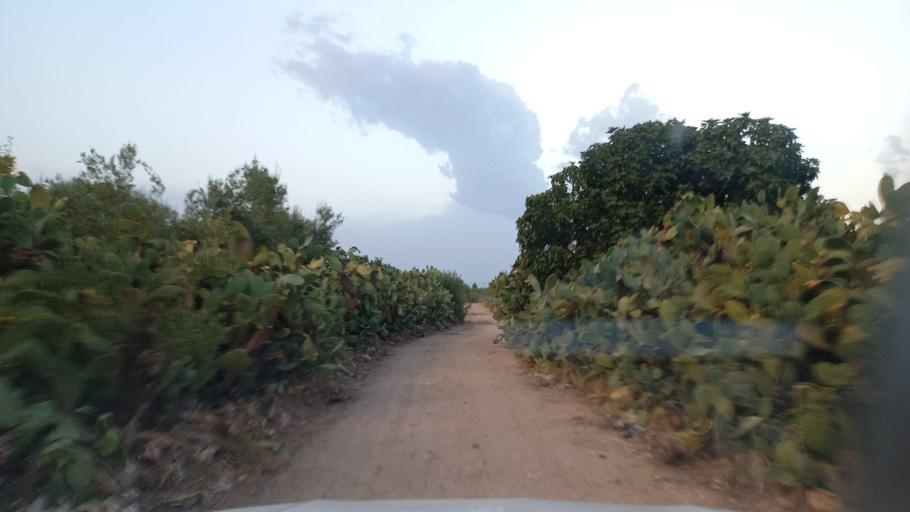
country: TN
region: Al Qasrayn
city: Kasserine
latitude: 35.2801
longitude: 9.0493
